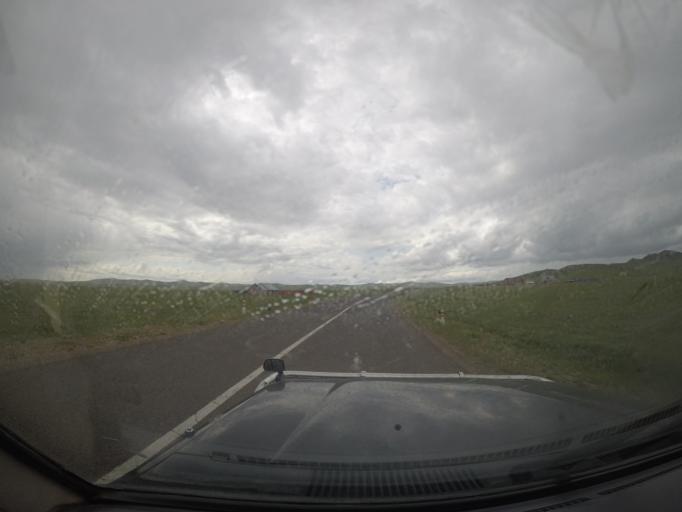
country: MN
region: Hentiy
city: Avraga
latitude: 47.4882
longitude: 109.4604
